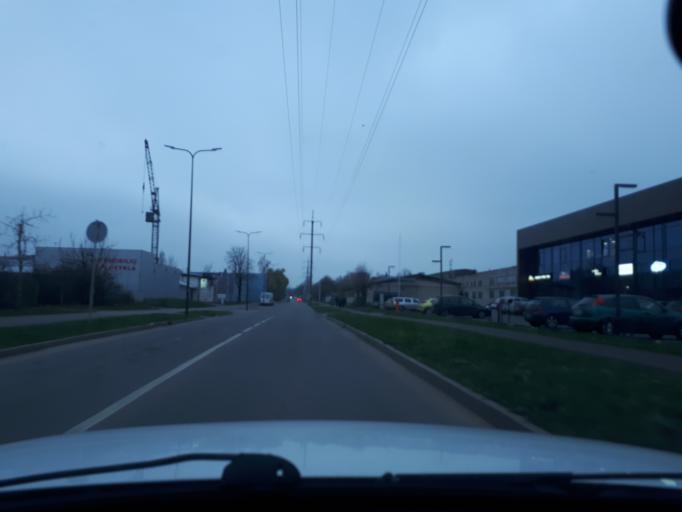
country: LT
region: Kauno apskritis
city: Dainava (Kaunas)
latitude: 54.9171
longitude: 23.9530
